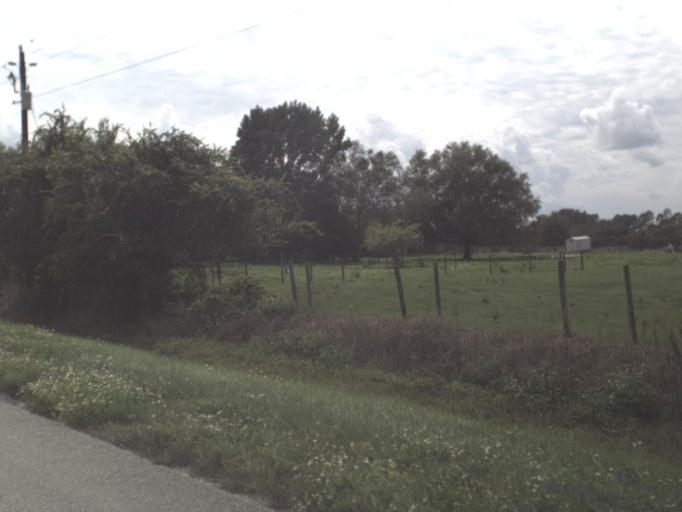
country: US
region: Florida
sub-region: DeSoto County
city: Nocatee
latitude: 27.0736
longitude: -81.7953
